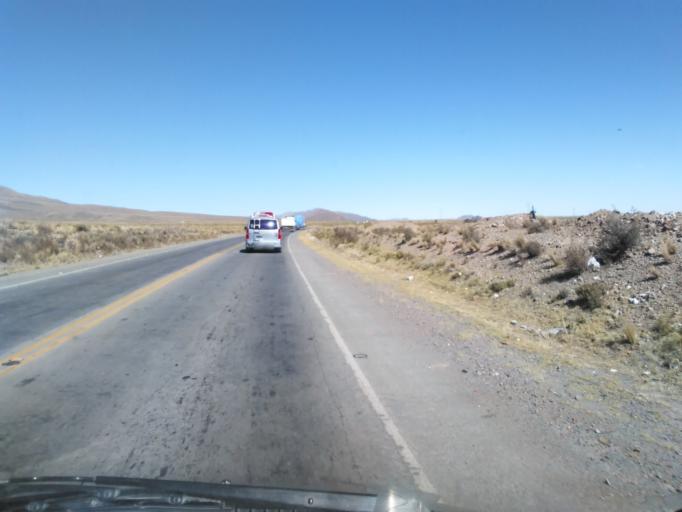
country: BO
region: Oruro
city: Machacamarca
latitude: -18.0591
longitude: -67.0061
